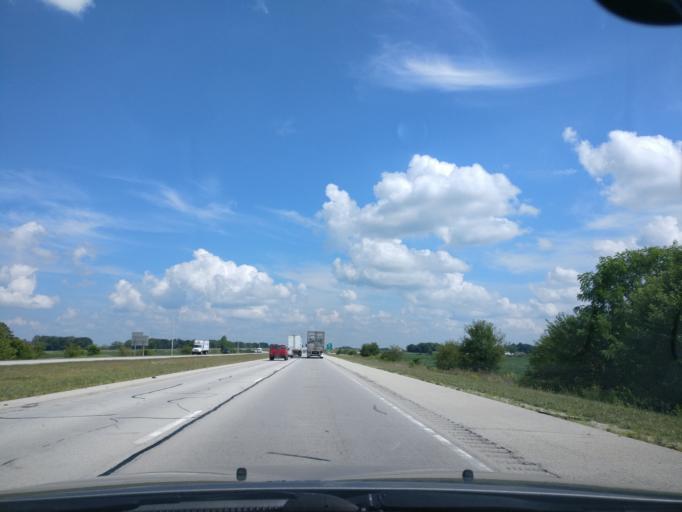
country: US
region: Ohio
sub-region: Greene County
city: Jamestown
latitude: 39.6723
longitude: -83.7469
